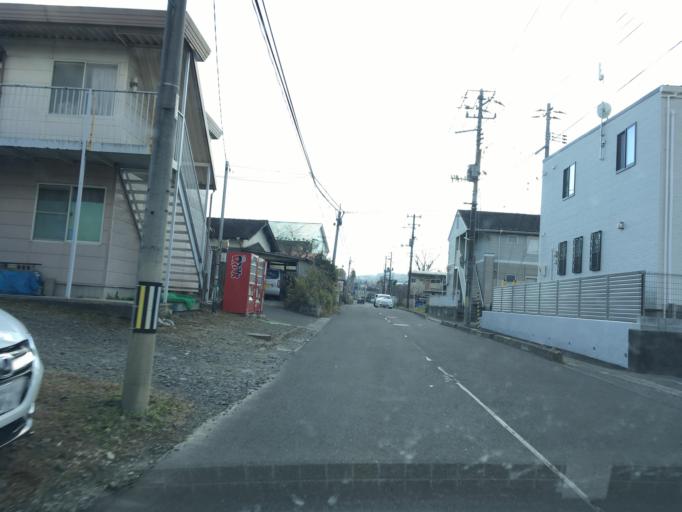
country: JP
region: Miyagi
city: Sendai
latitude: 38.2756
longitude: 140.7644
